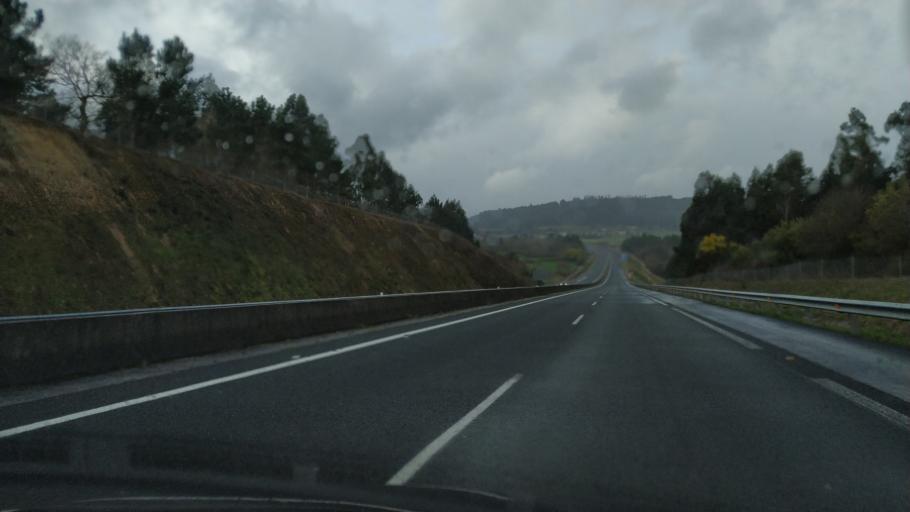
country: ES
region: Galicia
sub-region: Provincia de Pontevedra
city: Silleda
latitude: 42.7235
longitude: -8.3165
